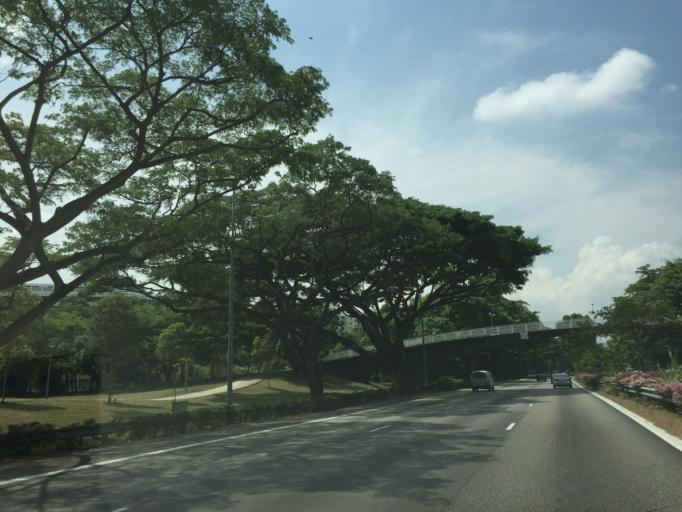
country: SG
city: Singapore
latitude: 1.3336
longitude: 103.9219
